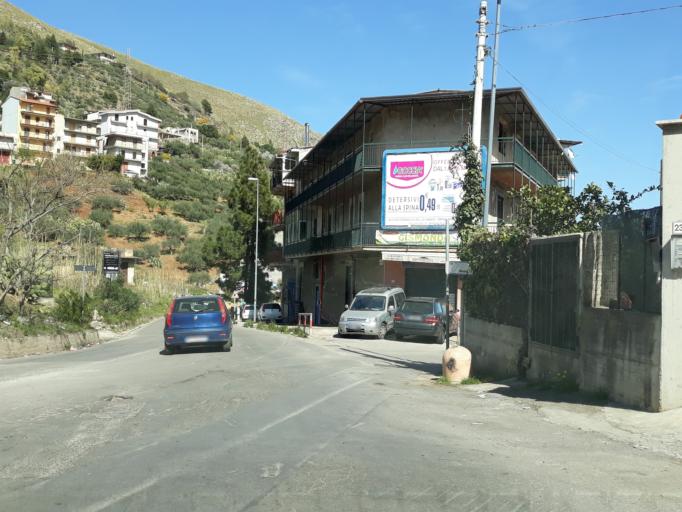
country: IT
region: Sicily
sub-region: Palermo
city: Belmonte Mezzagno
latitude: 38.0460
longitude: 13.3978
